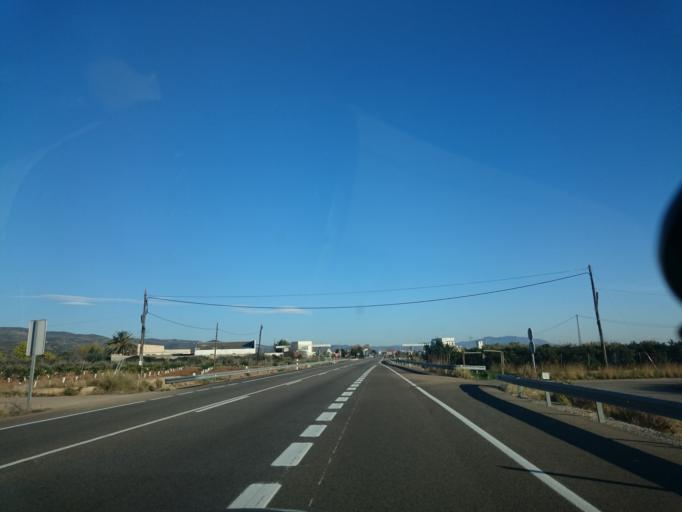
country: ES
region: Valencia
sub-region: Provincia de Castello
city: Orpesa/Oropesa del Mar
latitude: 40.1331
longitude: 0.1486
